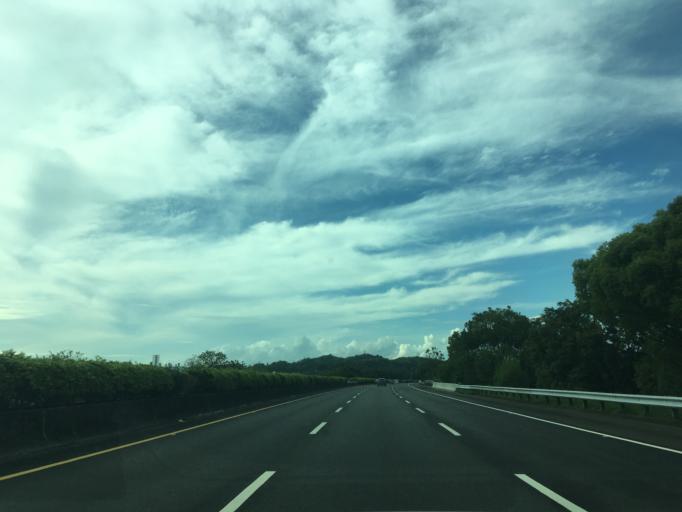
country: TW
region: Taiwan
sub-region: Chiayi
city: Jiayi Shi
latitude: 23.5147
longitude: 120.4855
